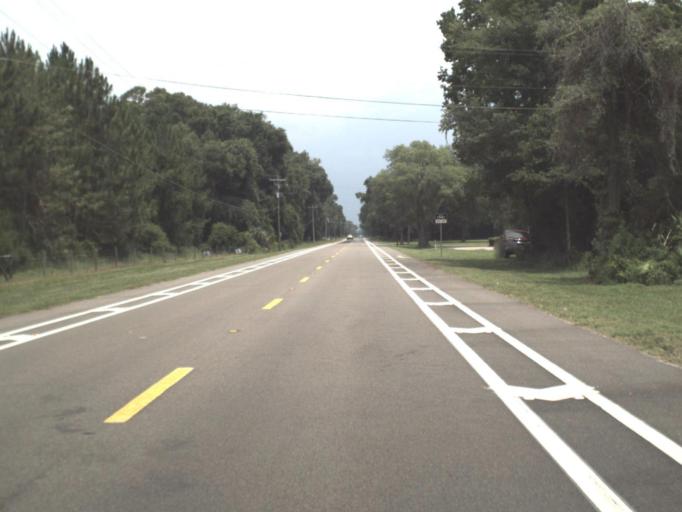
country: US
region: Florida
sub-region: Levy County
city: Manatee Road
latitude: 29.4963
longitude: -82.9344
